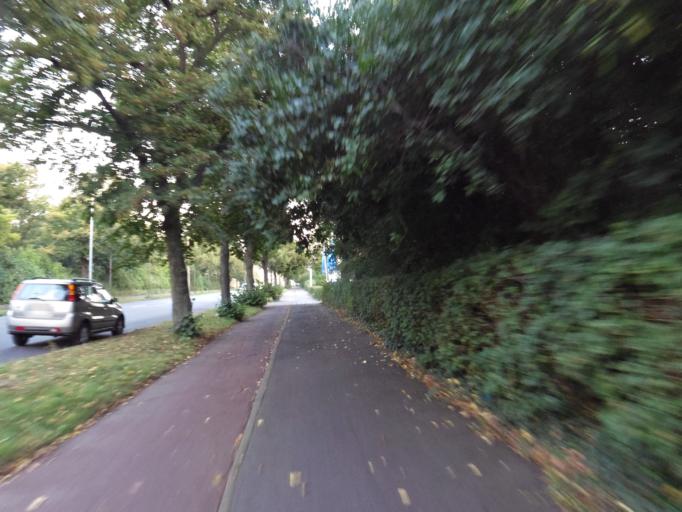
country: DE
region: Saxony
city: Leipzig
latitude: 51.3401
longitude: 12.3163
